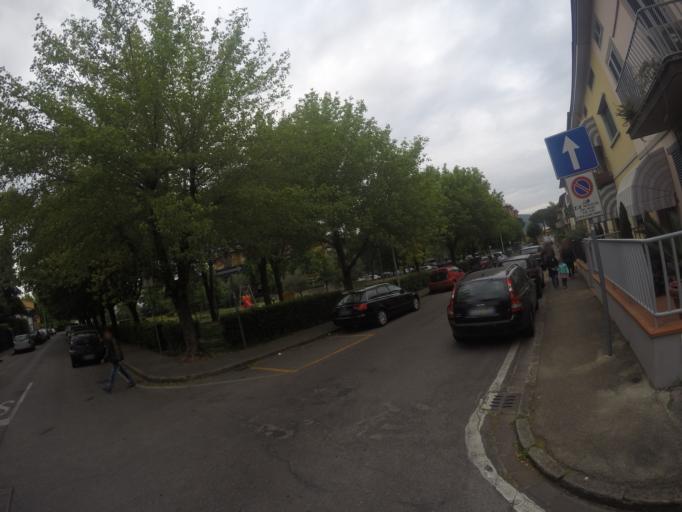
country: IT
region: Tuscany
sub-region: Provincia di Prato
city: Fornacelle
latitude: 43.8965
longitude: 11.0632
